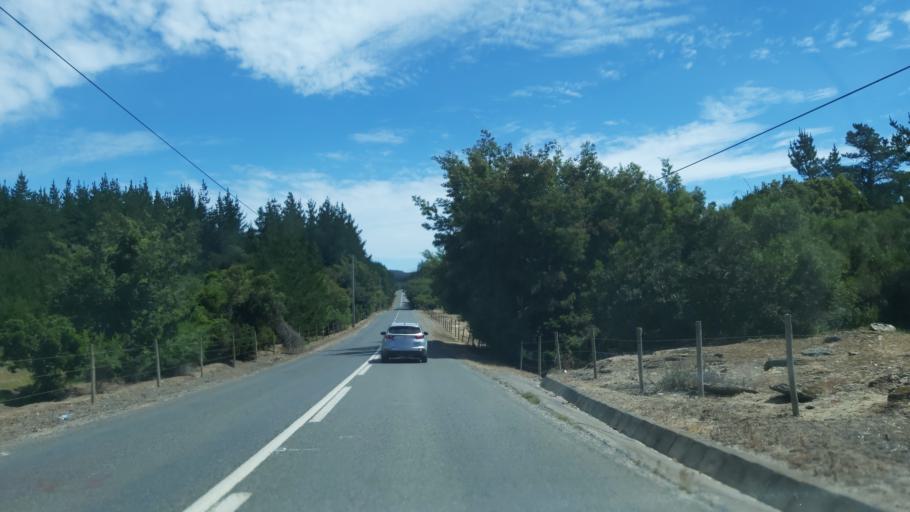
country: CL
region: Maule
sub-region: Provincia de Talca
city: Constitucion
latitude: -35.5246
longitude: -72.5375
